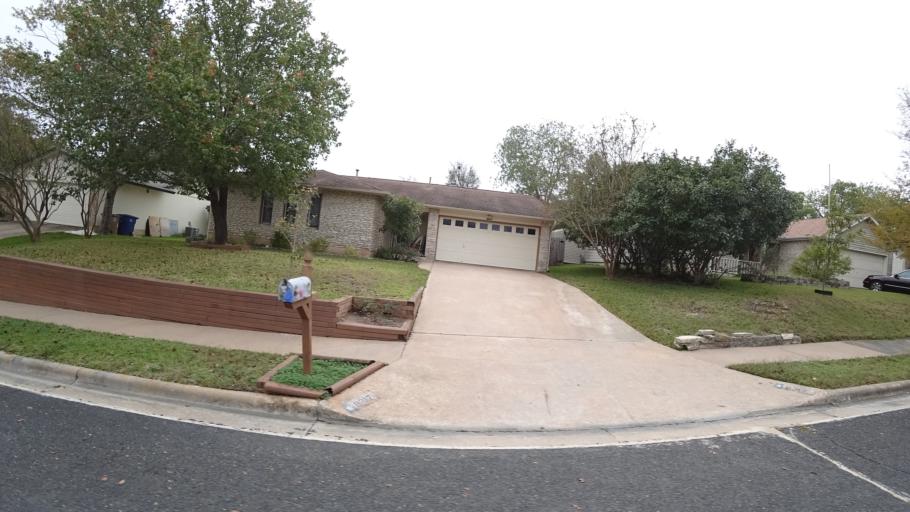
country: US
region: Texas
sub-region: Travis County
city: Barton Creek
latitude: 30.2386
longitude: -97.8964
